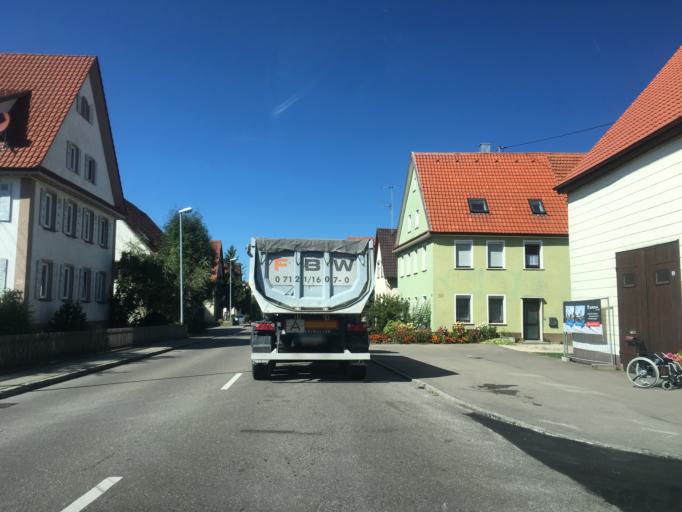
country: DE
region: Baden-Wuerttemberg
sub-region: Tuebingen Region
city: Sankt Johann
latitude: 48.3862
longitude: 9.2959
